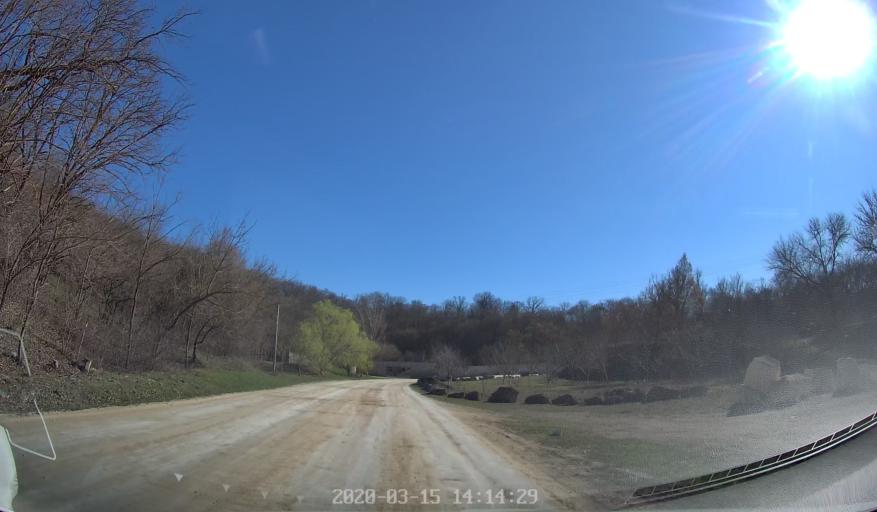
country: MD
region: Orhei
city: Orhei
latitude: 47.3131
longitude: 28.9361
